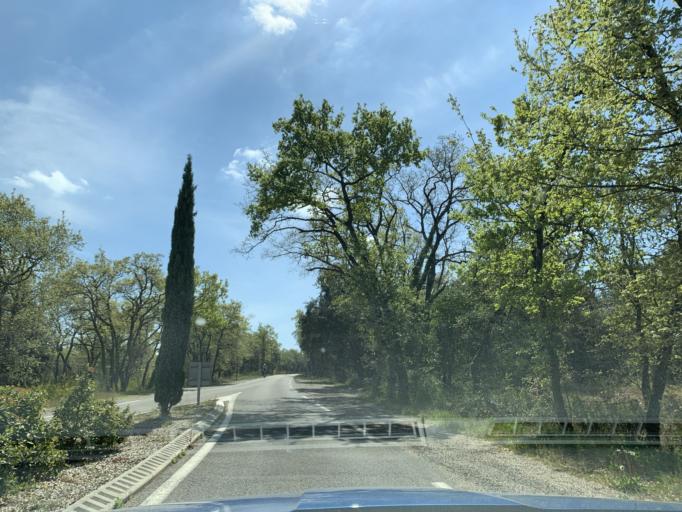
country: FR
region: Provence-Alpes-Cote d'Azur
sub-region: Departement du Vaucluse
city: Saint-Didier
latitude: 43.9746
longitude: 5.1137
